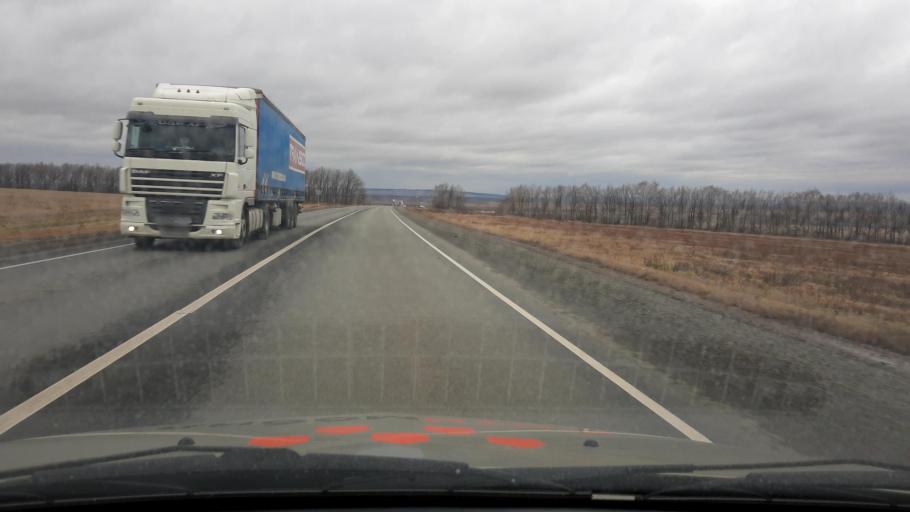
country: RU
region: Bashkortostan
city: Avdon
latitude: 54.8516
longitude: 55.7043
